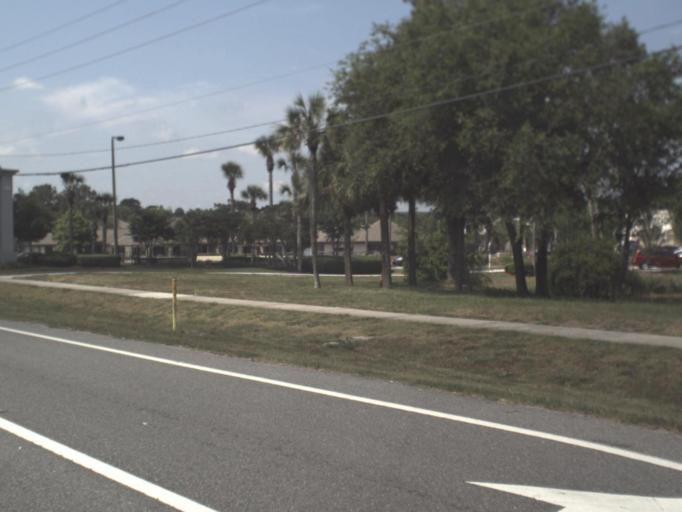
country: US
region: Florida
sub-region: Saint Johns County
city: Sawgrass
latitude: 30.2066
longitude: -81.3804
